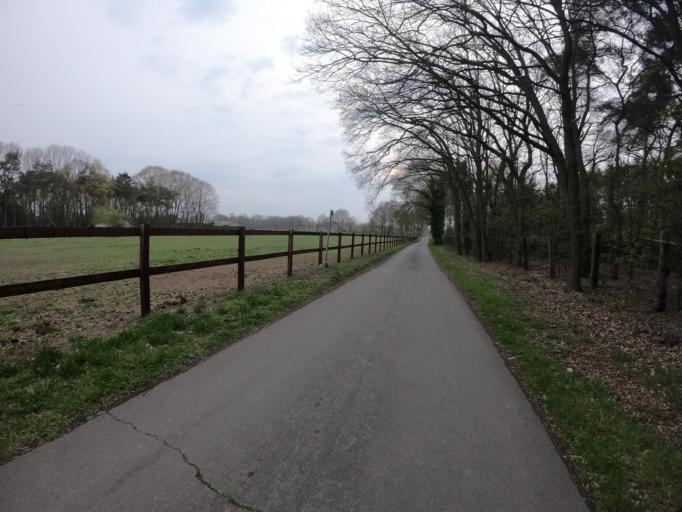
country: BE
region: Flanders
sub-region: Provincie Limburg
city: Maaseik
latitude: 51.0849
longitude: 5.7565
